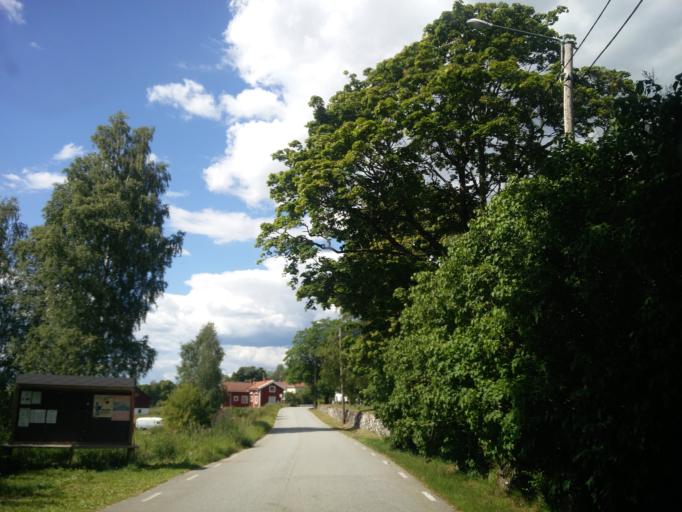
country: SE
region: OErebro
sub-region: Ljusnarsbergs Kommun
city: Kopparberg
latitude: 59.7833
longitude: 14.7794
